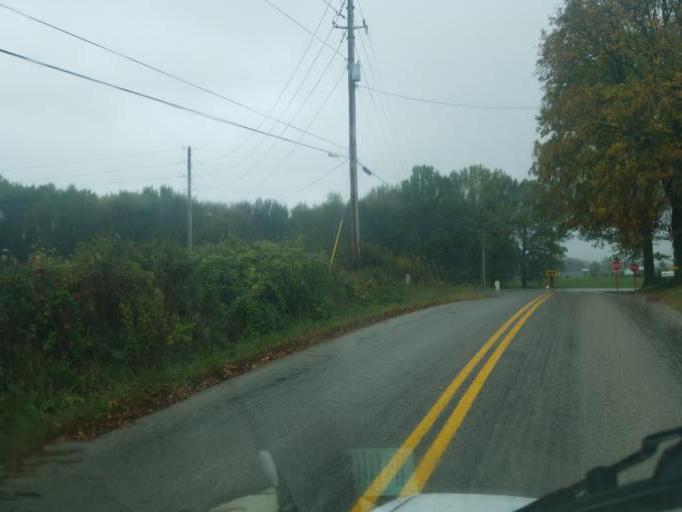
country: US
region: Ohio
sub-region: Wayne County
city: Shreve
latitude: 40.6368
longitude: -82.0203
